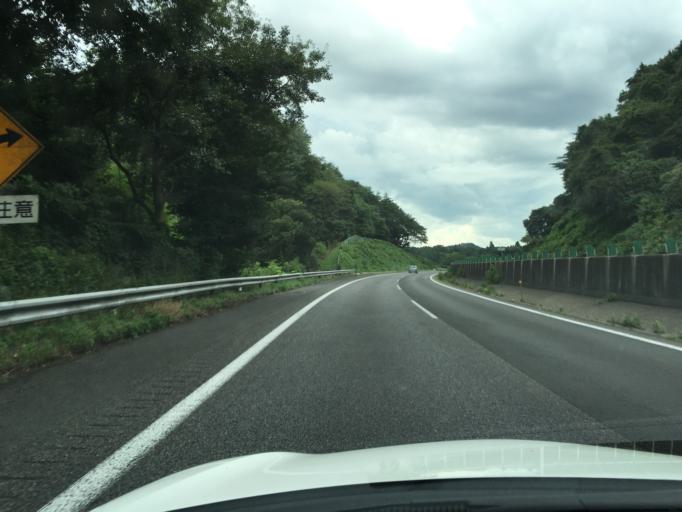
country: JP
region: Fukushima
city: Nihommatsu
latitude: 37.6264
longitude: 140.4318
